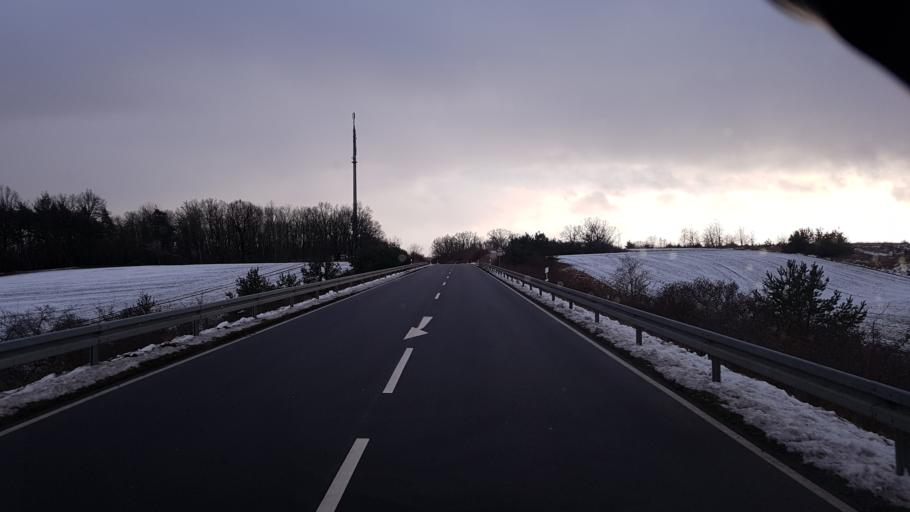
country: DE
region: Brandenburg
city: Heinersbruck
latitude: 51.8429
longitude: 14.5858
